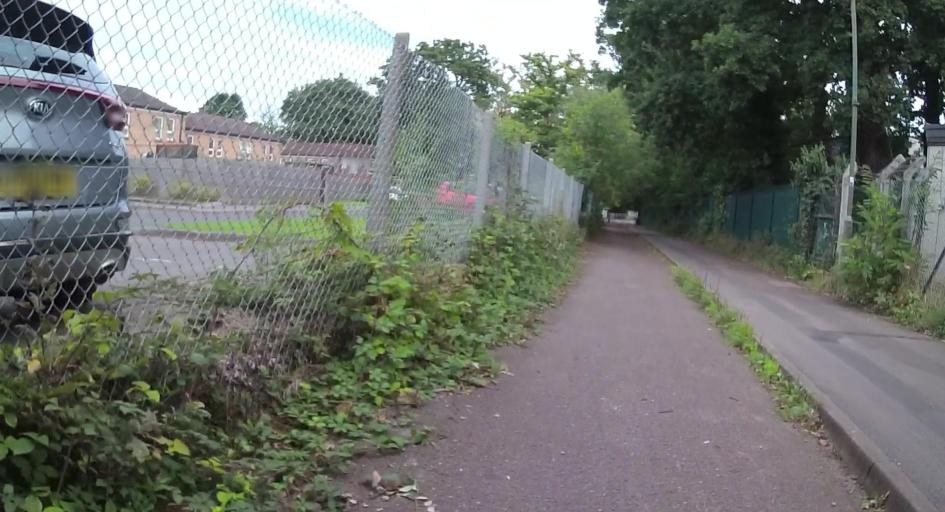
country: GB
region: England
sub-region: Surrey
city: Knaphill
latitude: 51.3135
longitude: -0.6012
